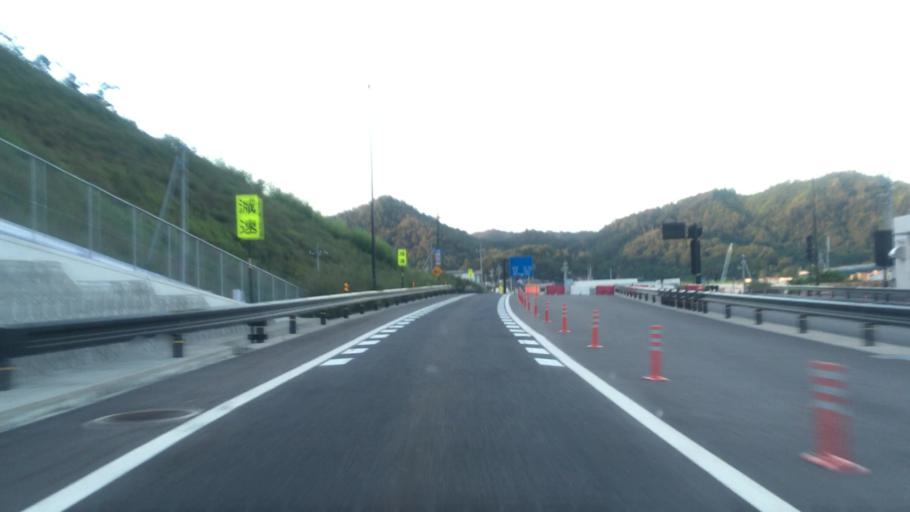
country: JP
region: Tottori
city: Tottori
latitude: 35.5805
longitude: 134.3303
